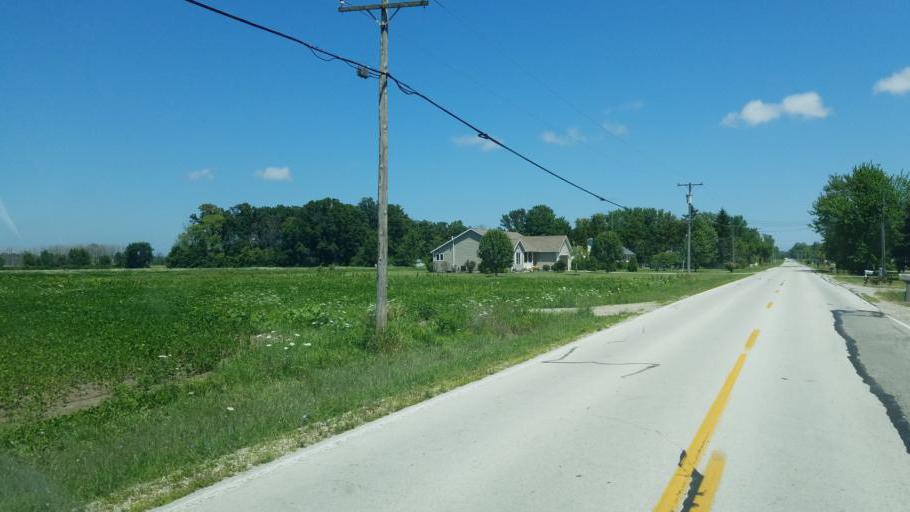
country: US
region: Ohio
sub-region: Ottawa County
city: Port Clinton
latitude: 41.4940
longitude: -82.9172
